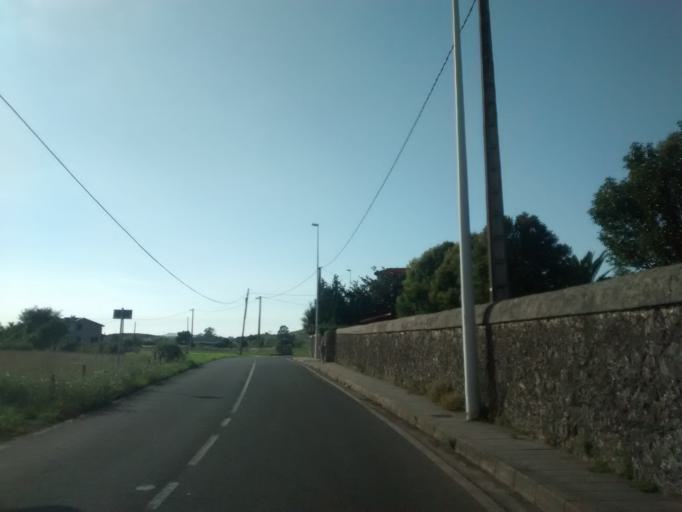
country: ES
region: Cantabria
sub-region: Provincia de Cantabria
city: Lierganes
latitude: 43.3992
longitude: -3.7356
